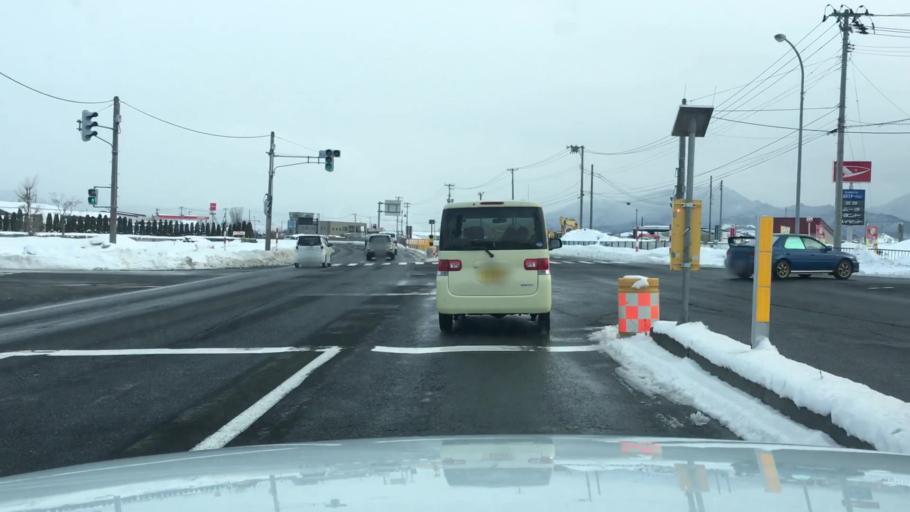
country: JP
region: Aomori
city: Hirosaki
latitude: 40.5857
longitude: 140.5077
